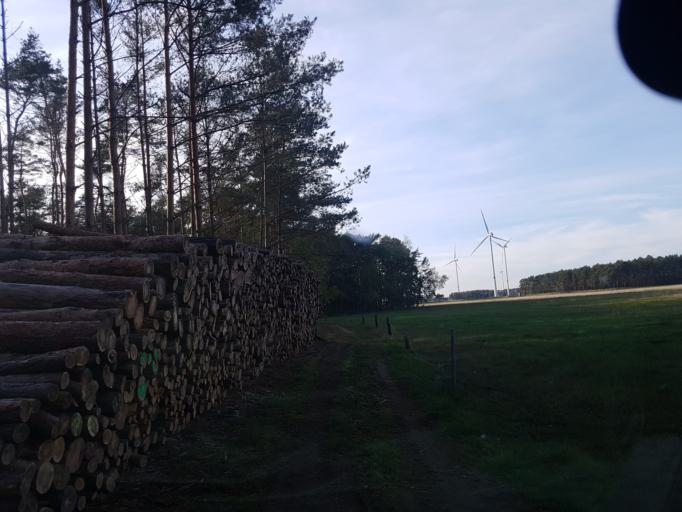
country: DE
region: Brandenburg
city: Schilda
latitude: 51.5664
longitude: 13.3266
